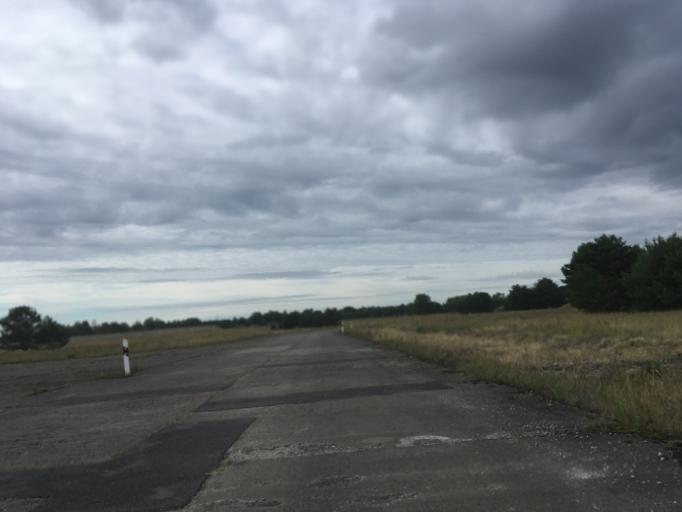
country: DE
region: Brandenburg
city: Halbe
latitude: 52.0408
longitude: 13.7380
